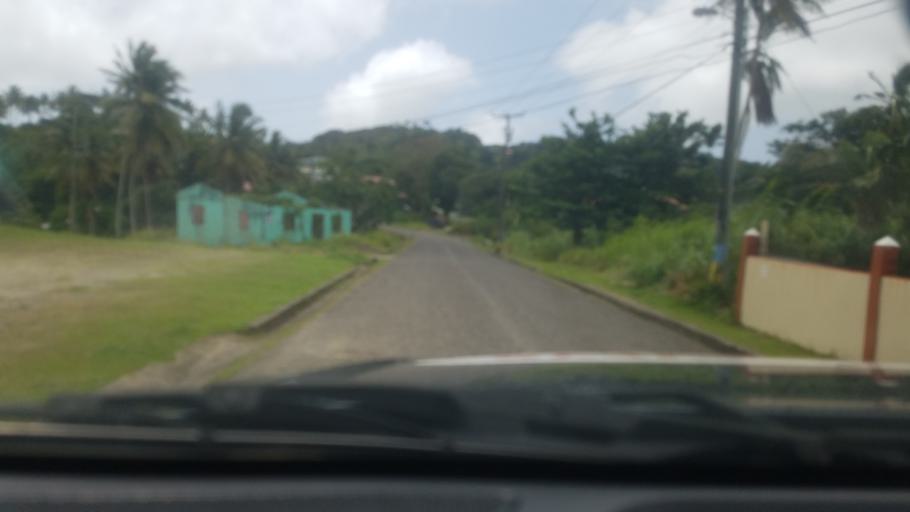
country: LC
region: Laborie Quarter
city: Laborie
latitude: 13.7916
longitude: -60.9551
